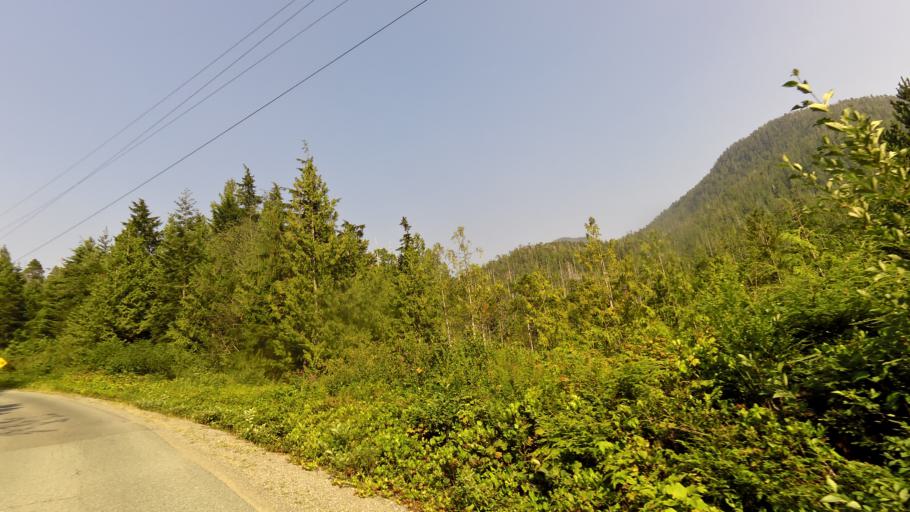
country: CA
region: British Columbia
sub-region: Regional District of Alberni-Clayoquot
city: Ucluelet
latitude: 49.1102
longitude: -125.4535
